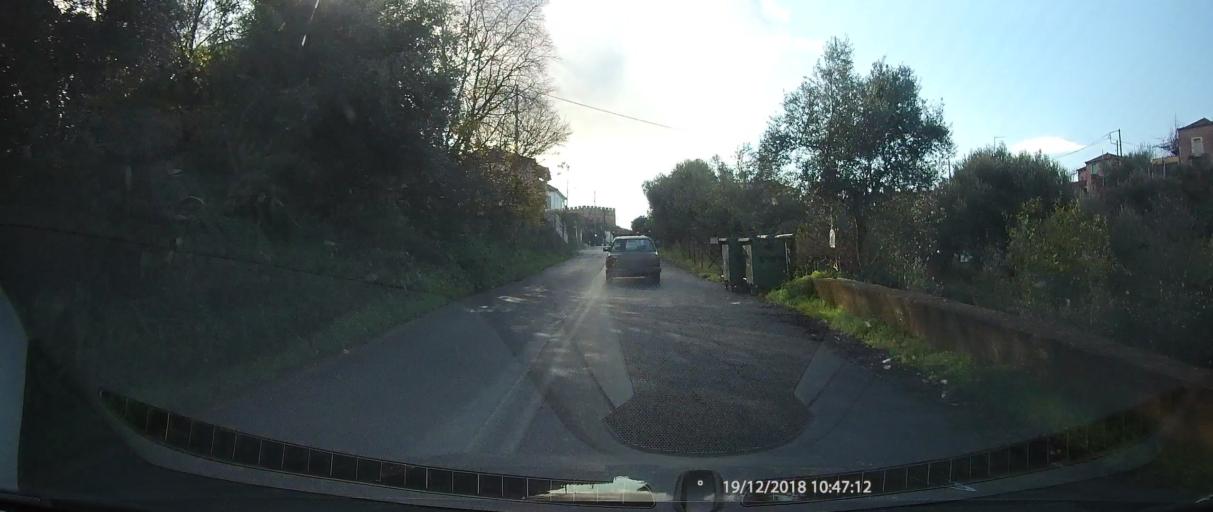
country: GR
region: Peloponnese
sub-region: Nomos Messinias
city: Kardamyli
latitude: 36.9375
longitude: 22.1916
